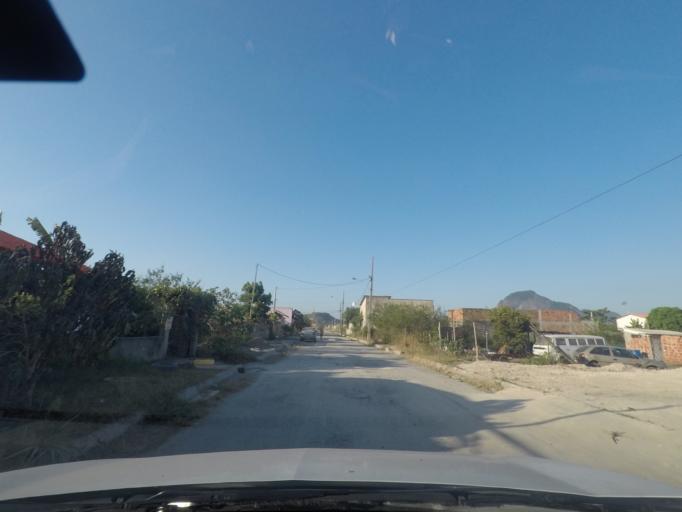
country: BR
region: Rio de Janeiro
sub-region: Marica
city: Marica
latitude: -22.9629
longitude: -42.9352
